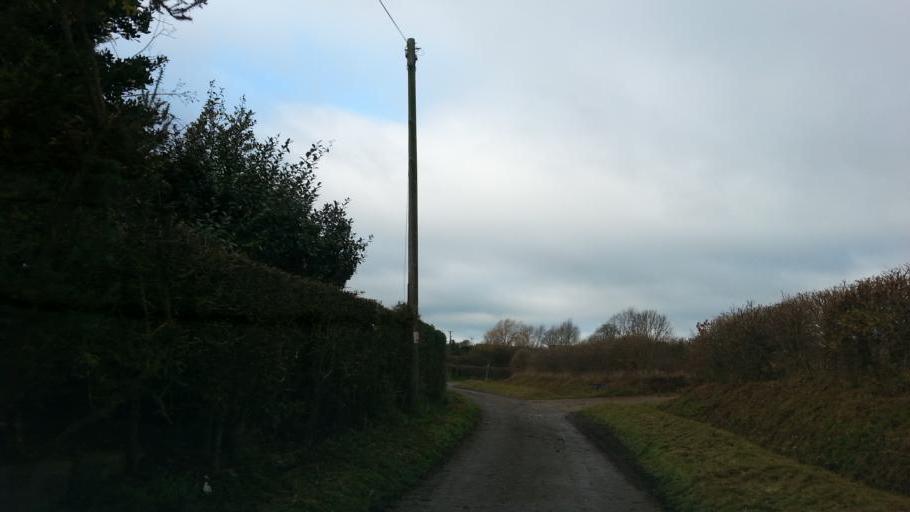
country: GB
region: England
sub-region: Suffolk
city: Cookley
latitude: 52.3035
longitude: 1.3668
